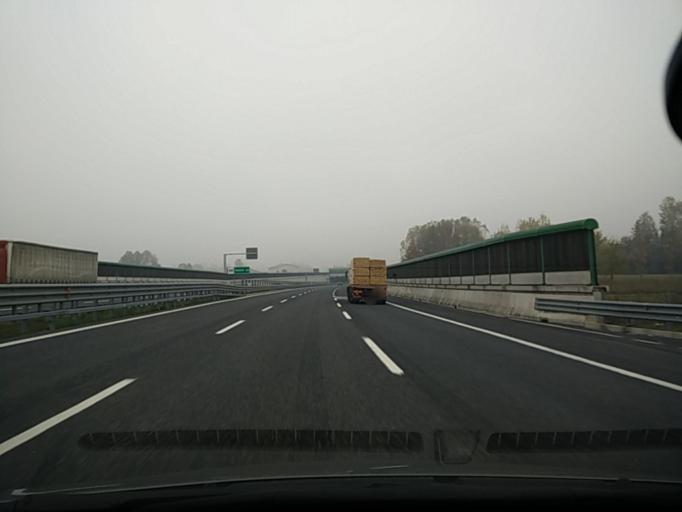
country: IT
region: Veneto
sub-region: Provincia di Venezia
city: Martellago
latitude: 45.5639
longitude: 12.1512
